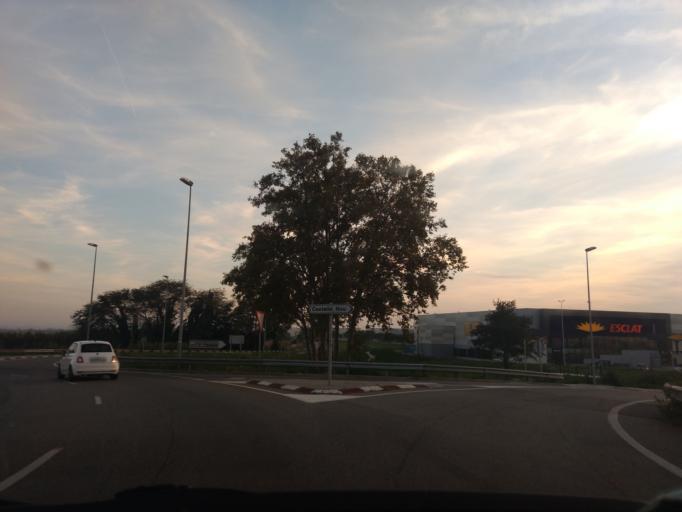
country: ES
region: Catalonia
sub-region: Provincia de Girona
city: Castello d'Empuries
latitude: 42.2514
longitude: 3.0757
